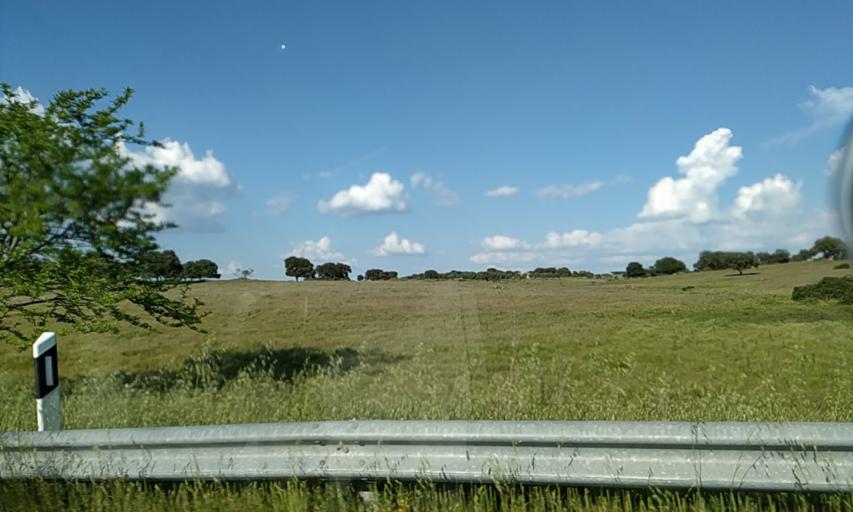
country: PT
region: Portalegre
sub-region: Portalegre
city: Urra
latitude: 39.1084
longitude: -7.4392
